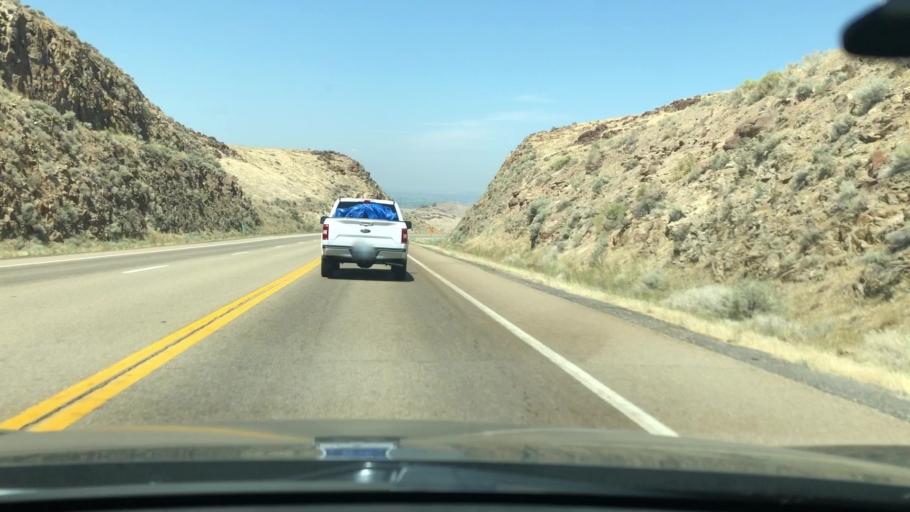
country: US
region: Idaho
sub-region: Owyhee County
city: Marsing
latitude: 43.4301
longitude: -116.8599
